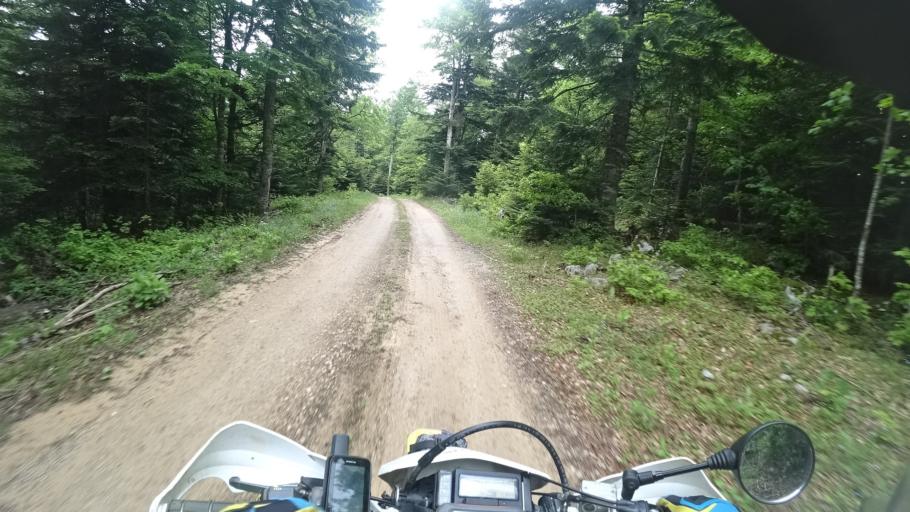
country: BA
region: Federation of Bosnia and Herzegovina
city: Bihac
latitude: 44.7019
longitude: 15.8295
